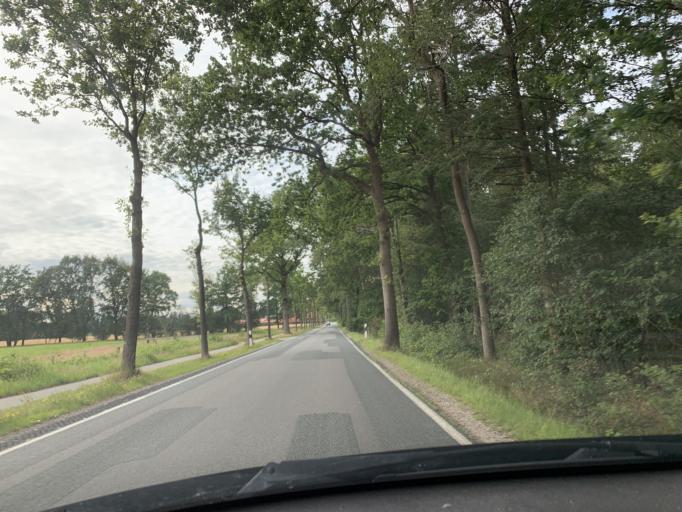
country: DE
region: Lower Saxony
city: Westerstede
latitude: 53.2788
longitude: 7.9272
